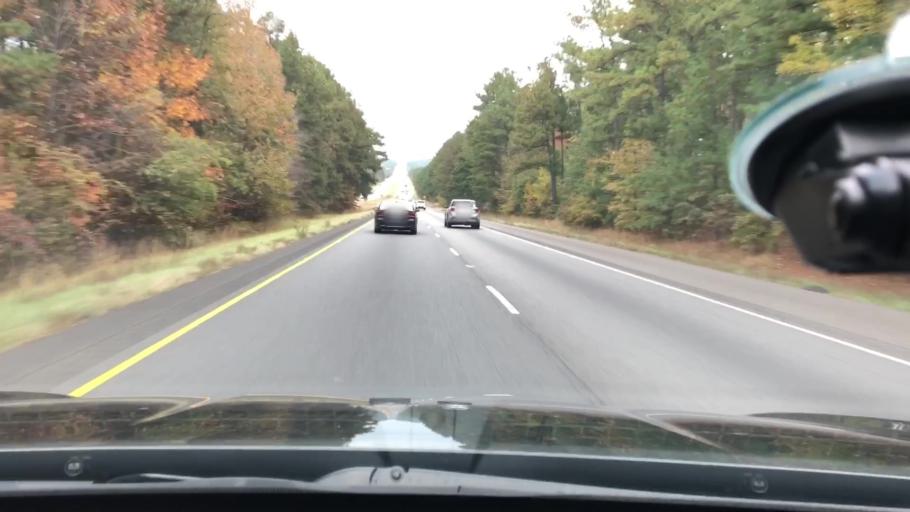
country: US
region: Arkansas
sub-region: Clark County
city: Arkadelphia
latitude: 34.2471
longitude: -92.9953
